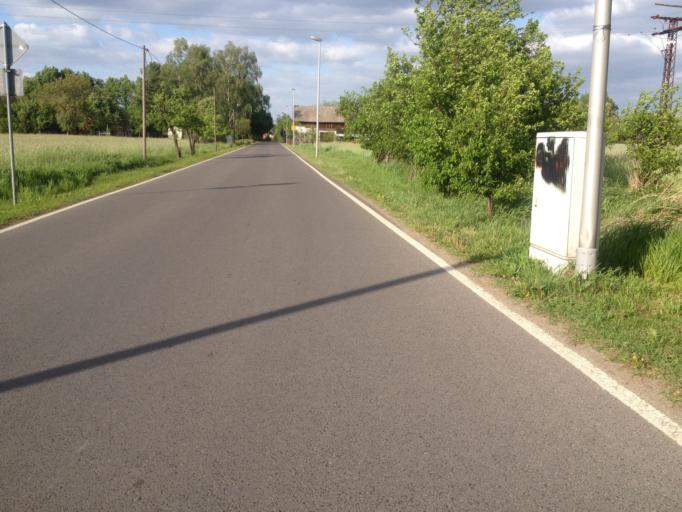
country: DE
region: Brandenburg
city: Cottbus
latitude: 51.8132
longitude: 14.3332
